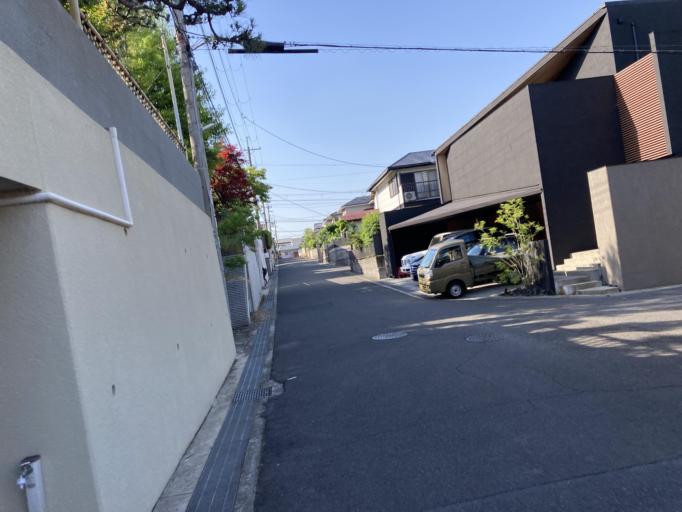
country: JP
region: Nara
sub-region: Ikoma-shi
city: Ikoma
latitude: 34.7101
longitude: 135.7199
